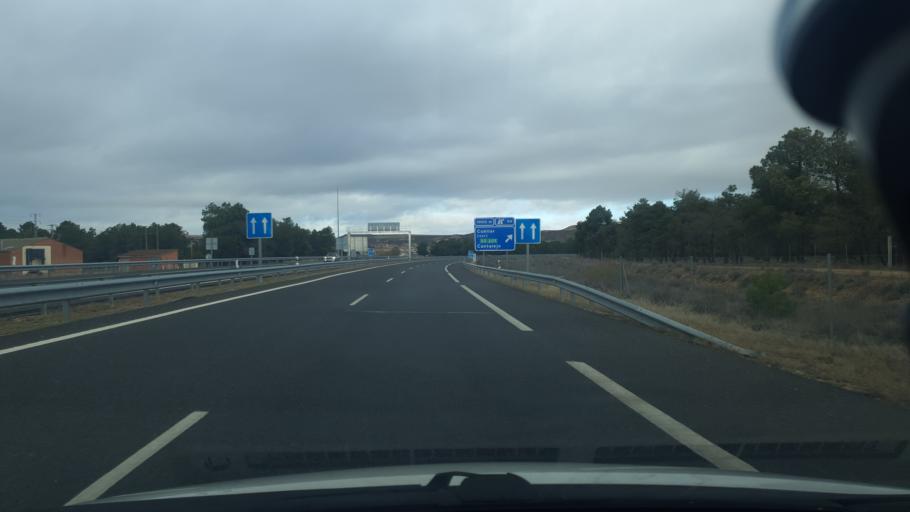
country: ES
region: Castille and Leon
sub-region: Provincia de Segovia
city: Cuellar
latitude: 41.3763
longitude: -4.3008
